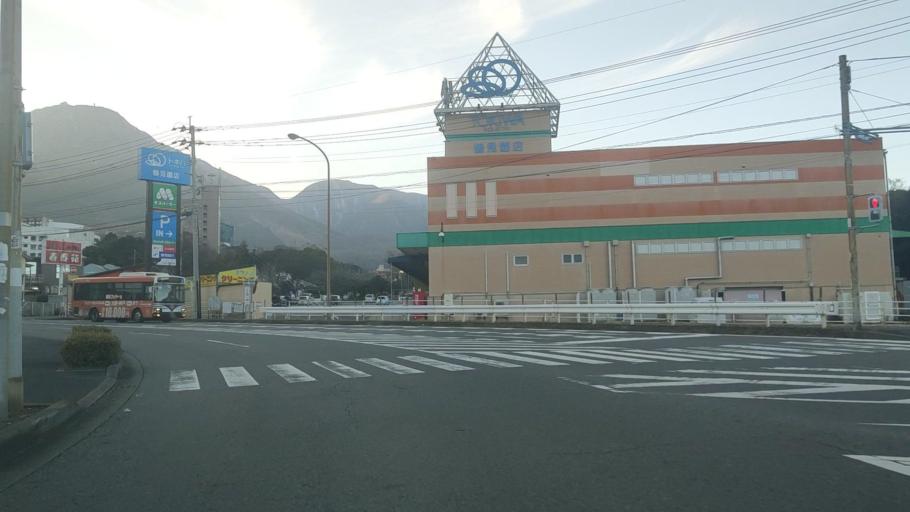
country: JP
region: Oita
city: Beppu
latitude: 33.2847
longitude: 131.4802
